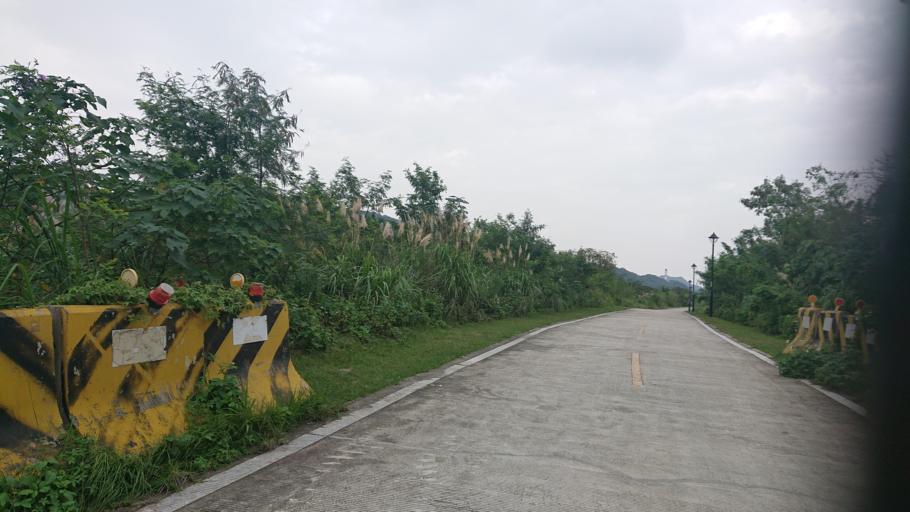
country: TW
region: Taiwan
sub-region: Taoyuan
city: Taoyuan
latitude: 24.9501
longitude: 121.3623
